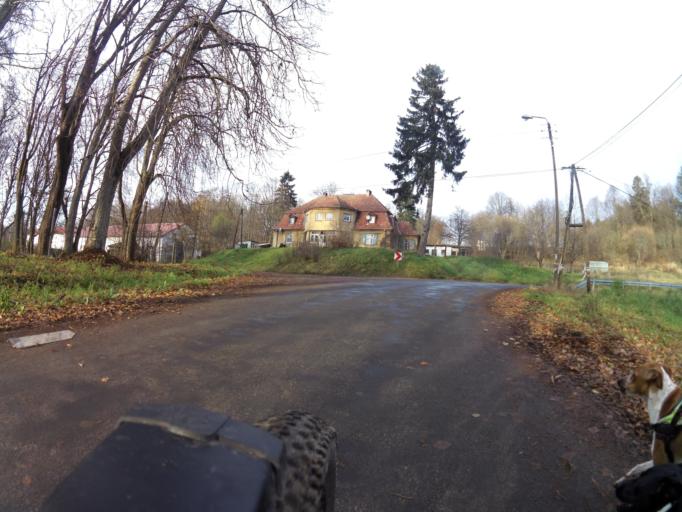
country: PL
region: West Pomeranian Voivodeship
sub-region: Powiat koszalinski
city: Polanow
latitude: 54.0802
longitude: 16.6672
